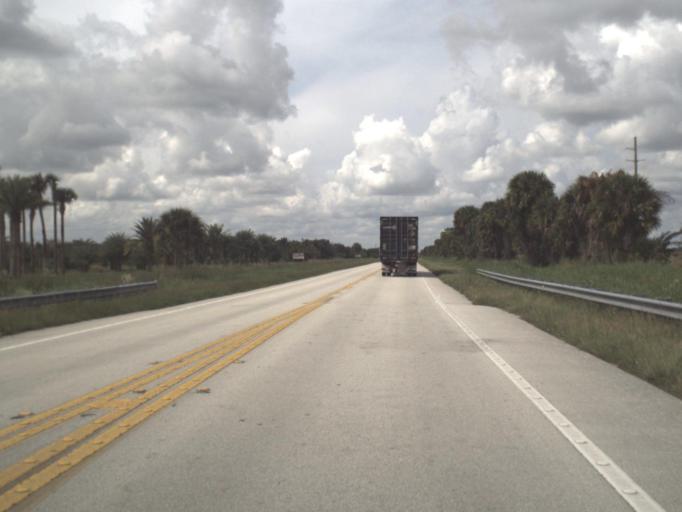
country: US
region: Florida
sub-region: Okeechobee County
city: Okeechobee
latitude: 27.2436
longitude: -80.9203
